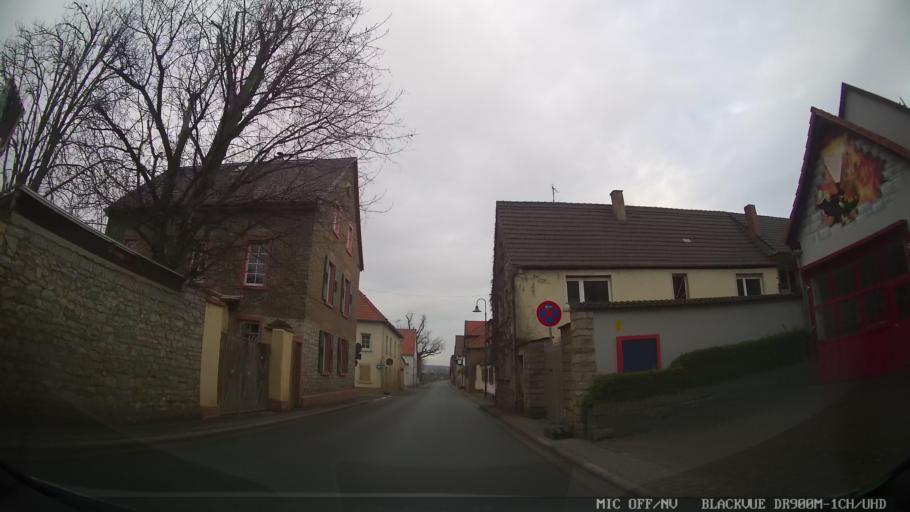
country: DE
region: Rheinland-Pfalz
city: Kongernheim
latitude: 49.8461
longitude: 8.2464
